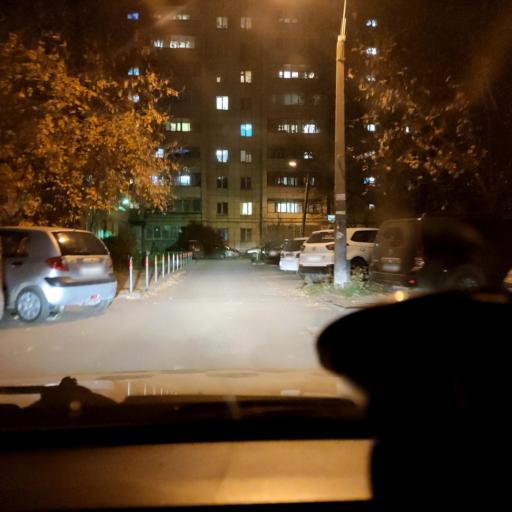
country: RU
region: Perm
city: Perm
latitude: 58.0044
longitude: 56.2790
